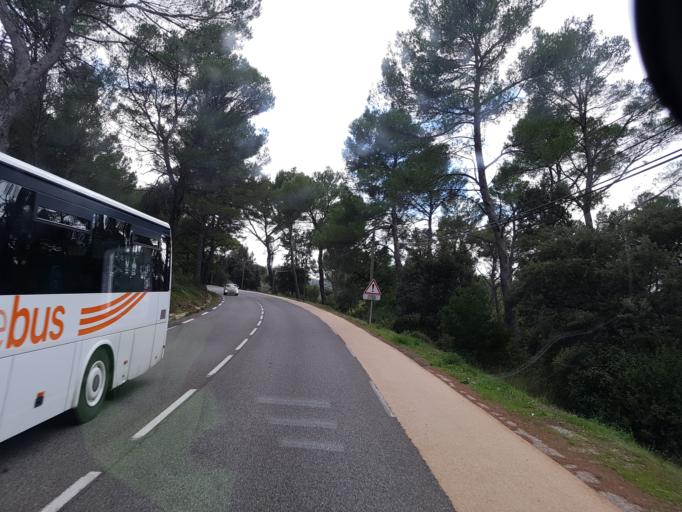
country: FR
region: Provence-Alpes-Cote d'Azur
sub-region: Departement des Bouches-du-Rhone
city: Cuges-les-Pins
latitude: 43.2726
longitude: 5.7193
